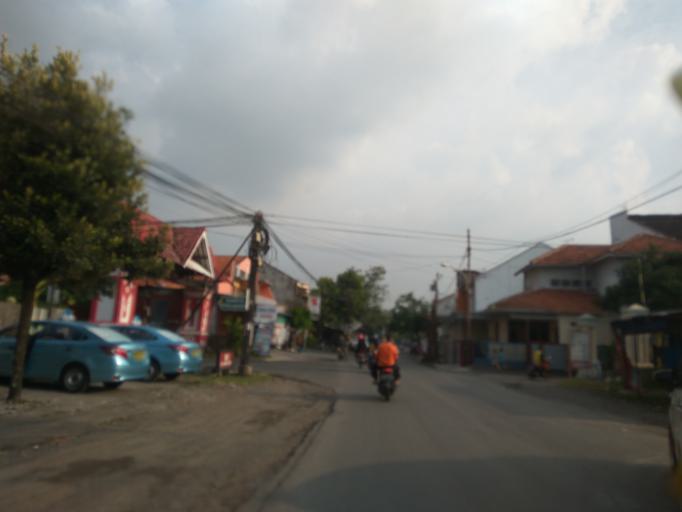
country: ID
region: Central Java
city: Semarang
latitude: -7.0129
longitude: 110.3951
